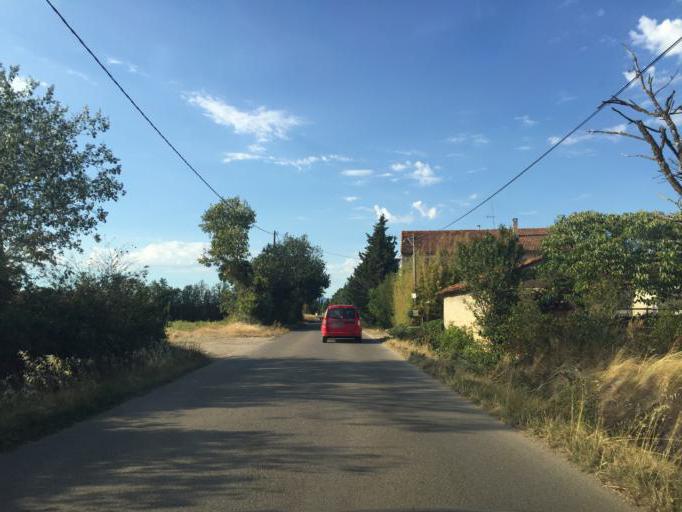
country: FR
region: Provence-Alpes-Cote d'Azur
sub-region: Departement du Vaucluse
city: Pernes-les-Fontaines
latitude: 44.0165
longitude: 5.0550
